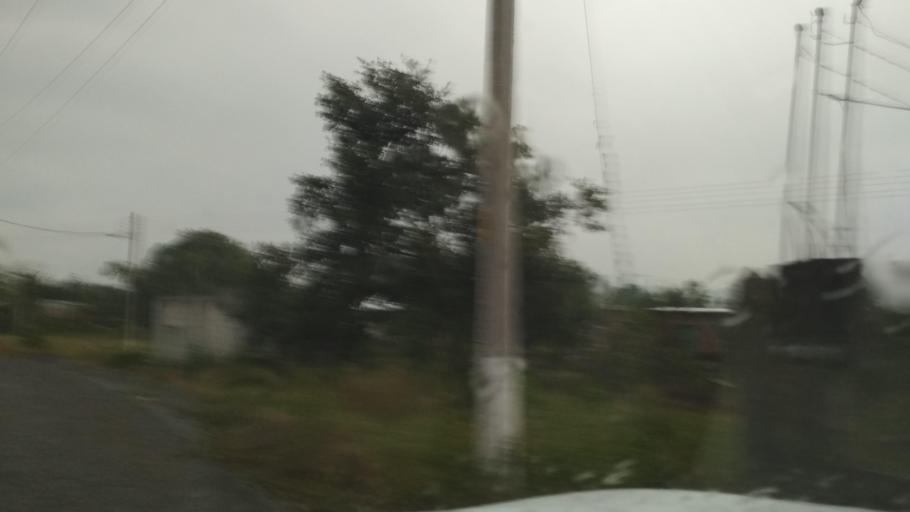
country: MM
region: Shan
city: Taunggyi
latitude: 20.3013
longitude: 97.3059
